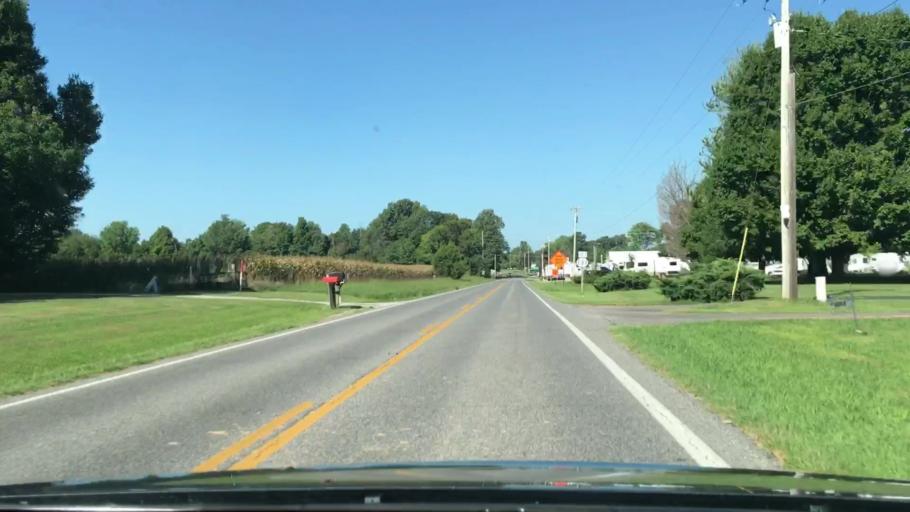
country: US
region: Kentucky
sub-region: Graves County
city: Mayfield
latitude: 36.7600
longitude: -88.5932
